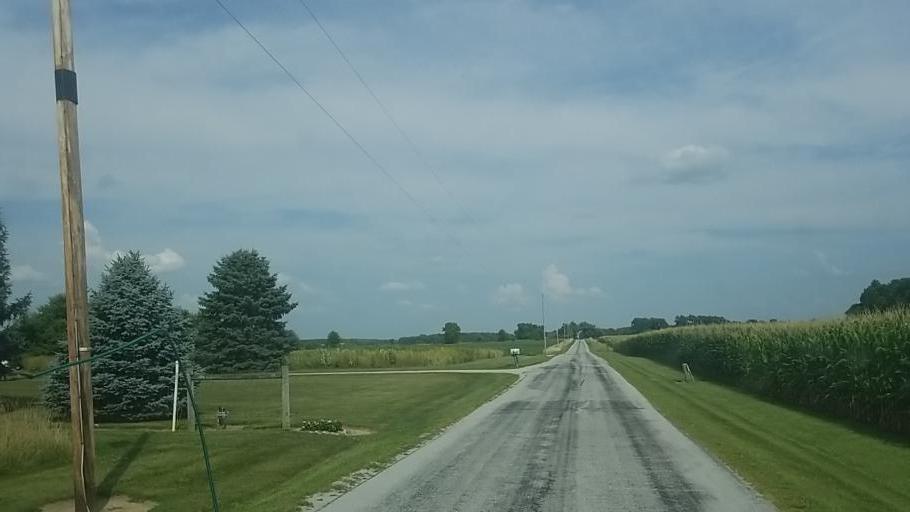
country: US
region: Ohio
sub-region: Hardin County
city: Forest
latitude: 40.8175
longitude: -83.4613
